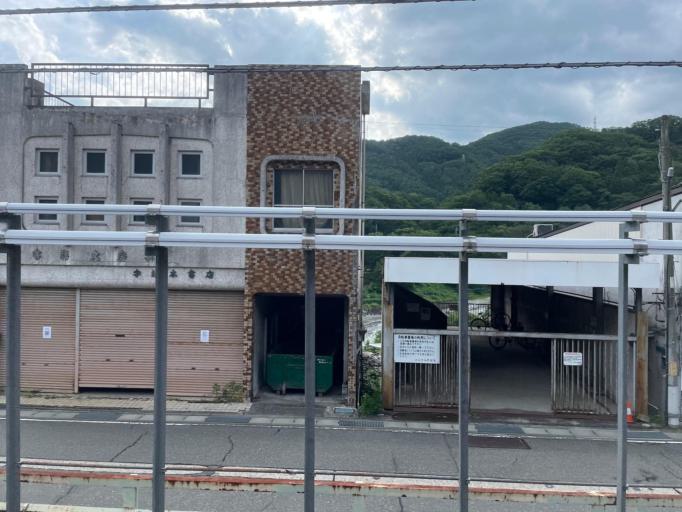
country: JP
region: Gunma
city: Numata
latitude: 36.7775
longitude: 138.9689
